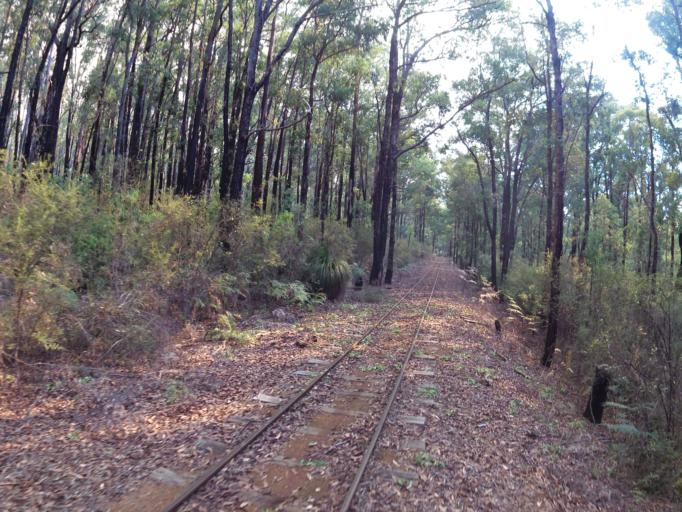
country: AU
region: Western Australia
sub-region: Waroona
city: Waroona
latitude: -32.7376
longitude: 116.1221
